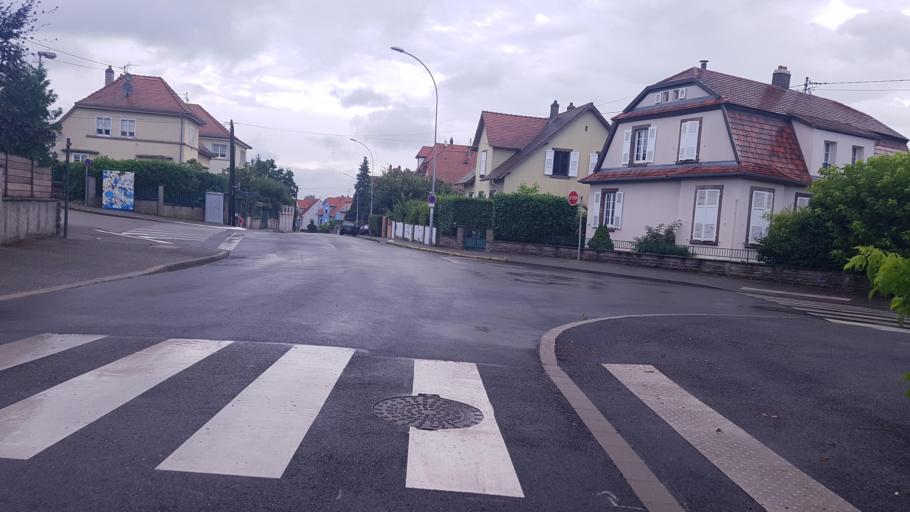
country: FR
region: Alsace
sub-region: Departement du Bas-Rhin
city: Saverne
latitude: 48.7339
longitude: 7.3610
